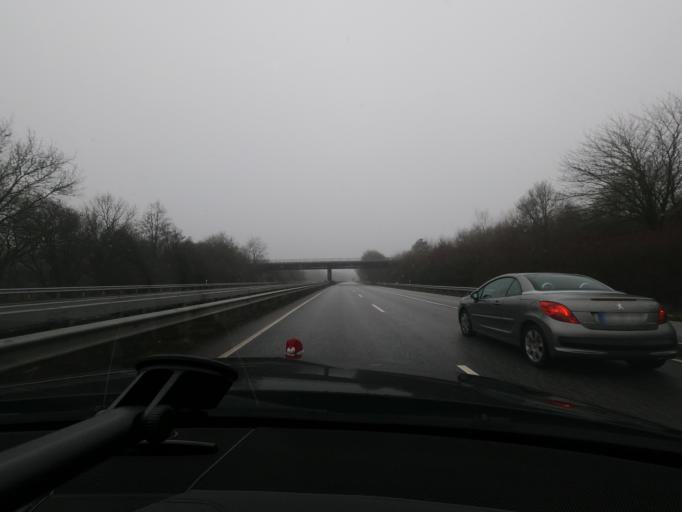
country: DE
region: Schleswig-Holstein
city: Jarplund-Weding
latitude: 54.7451
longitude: 9.4191
